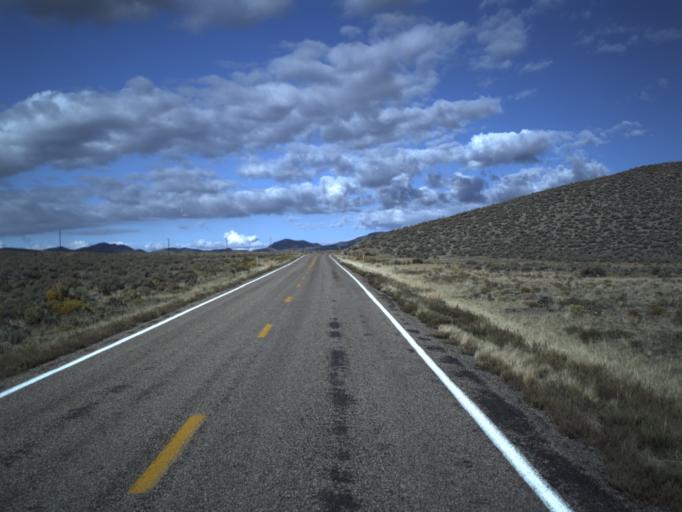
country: US
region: Utah
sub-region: Beaver County
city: Milford
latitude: 38.4237
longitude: -113.1102
